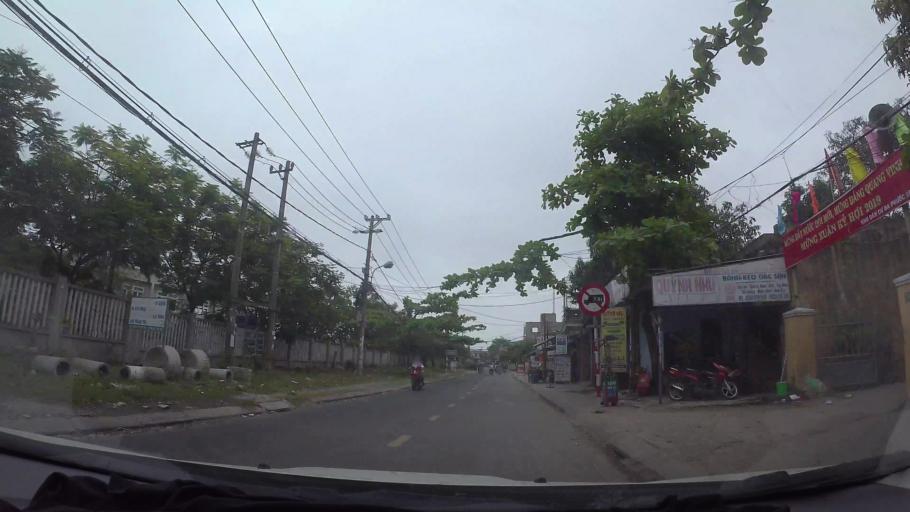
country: VN
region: Da Nang
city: Lien Chieu
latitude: 16.0718
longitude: 108.1402
